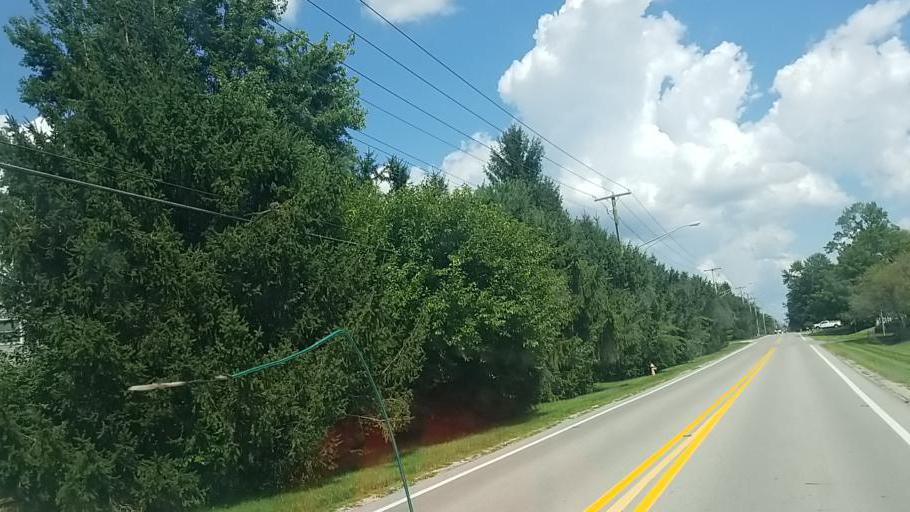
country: US
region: Ohio
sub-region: Franklin County
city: Worthington
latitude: 40.1270
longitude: -82.9985
